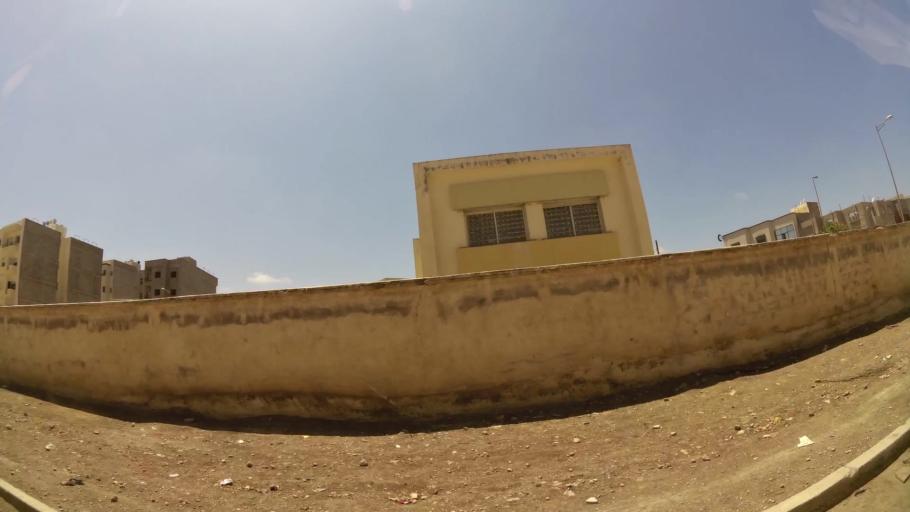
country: MA
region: Fes-Boulemane
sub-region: Fes
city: Fes
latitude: 34.0339
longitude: -5.0427
